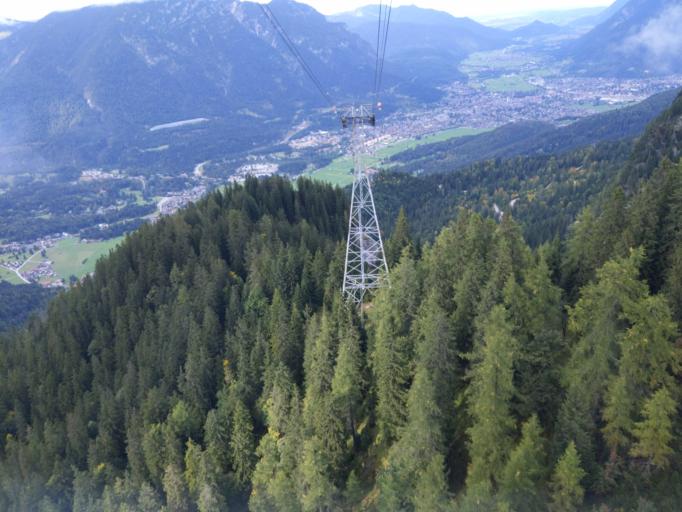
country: DE
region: Bavaria
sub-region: Upper Bavaria
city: Grainau
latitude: 47.4483
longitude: 11.0541
